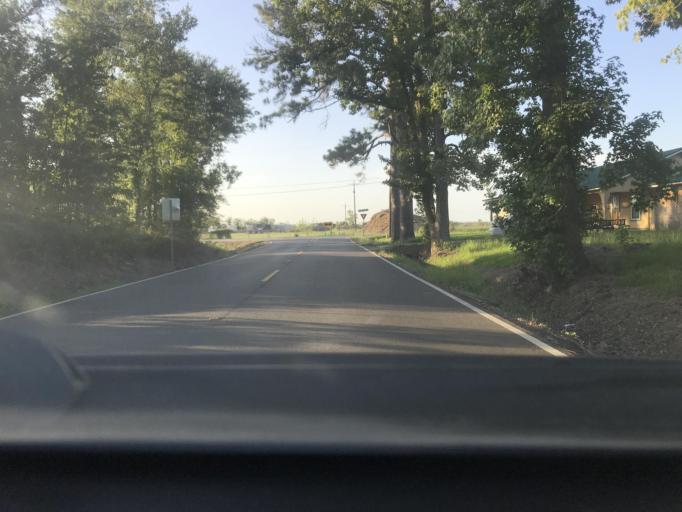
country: US
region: Louisiana
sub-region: Calcasieu Parish
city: Moss Bluff
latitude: 30.2633
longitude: -93.1953
